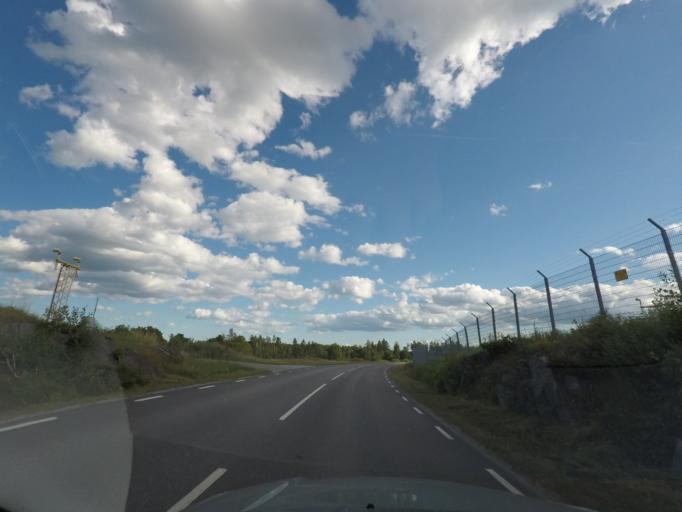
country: SE
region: Stockholm
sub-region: Sigtuna Kommun
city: Rosersberg
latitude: 59.6648
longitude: 17.9853
